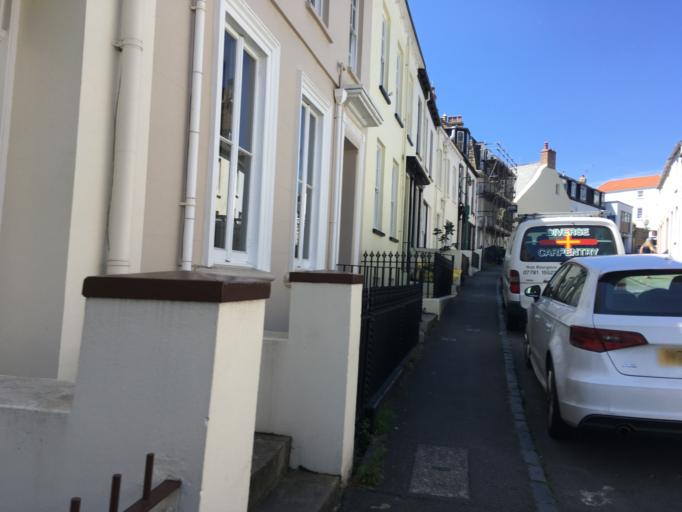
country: GG
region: St Peter Port
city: Saint Peter Port
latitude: 49.4548
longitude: -2.5466
